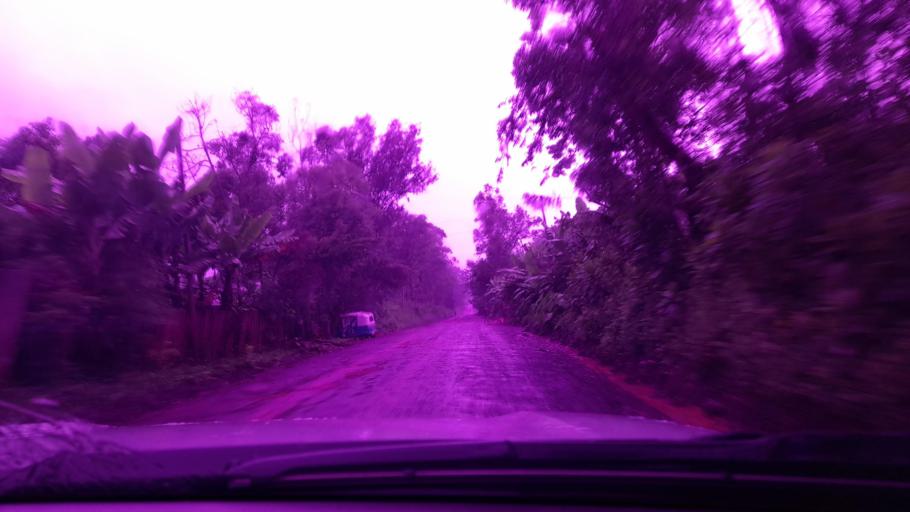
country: ET
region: Oromiya
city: Metu
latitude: 8.3182
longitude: 35.5990
